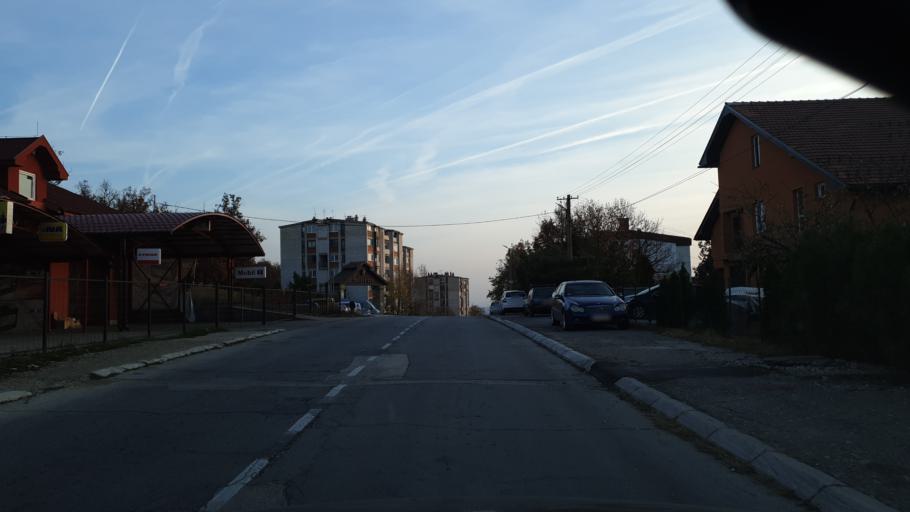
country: RS
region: Central Serbia
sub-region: Borski Okrug
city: Bor
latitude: 44.0597
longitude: 22.0954
